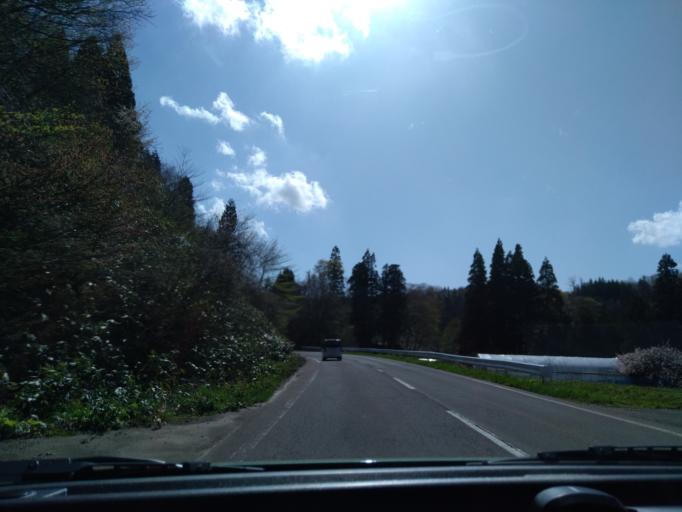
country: JP
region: Akita
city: Akita
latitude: 39.6942
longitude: 140.2300
